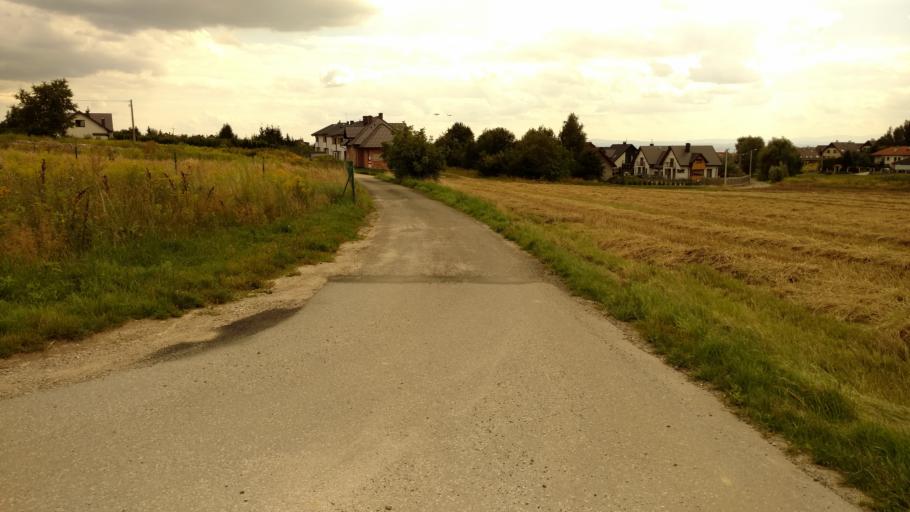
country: PL
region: Lesser Poland Voivodeship
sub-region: Powiat krakowski
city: Michalowice
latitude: 50.1360
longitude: 19.9616
